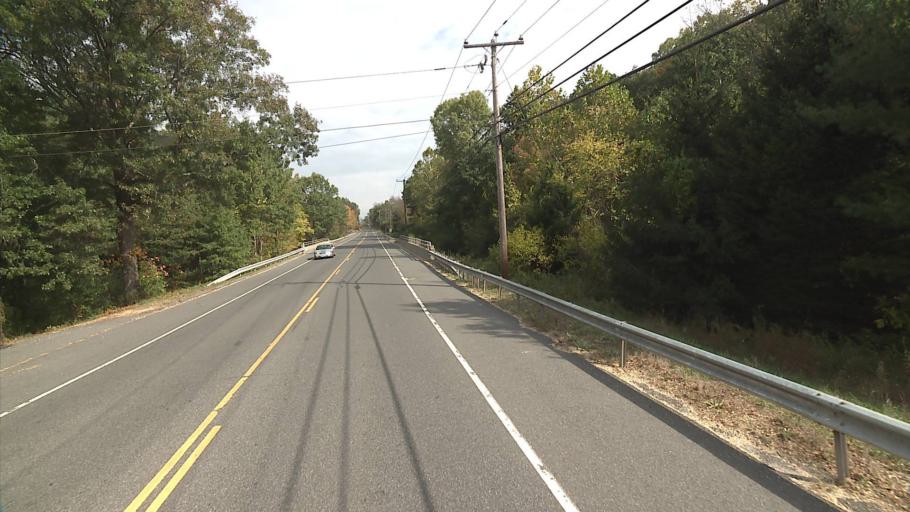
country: US
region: Connecticut
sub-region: Litchfield County
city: Woodbury Center
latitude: 41.5836
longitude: -73.1738
